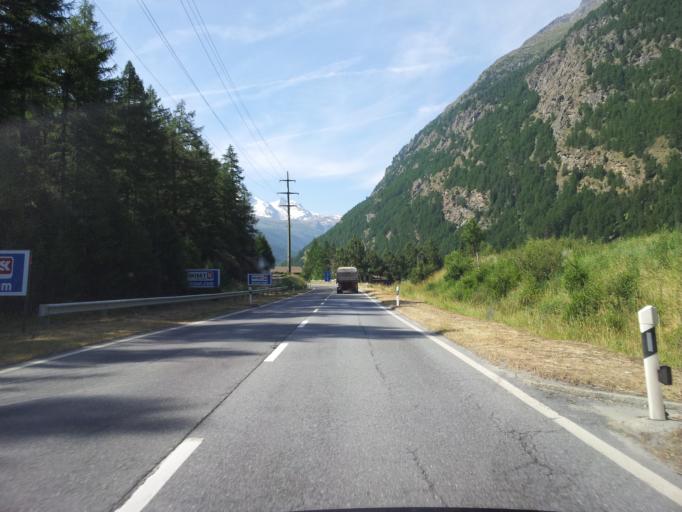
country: CH
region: Valais
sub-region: Visp District
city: Zermatt
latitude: 46.0830
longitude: 7.7801
